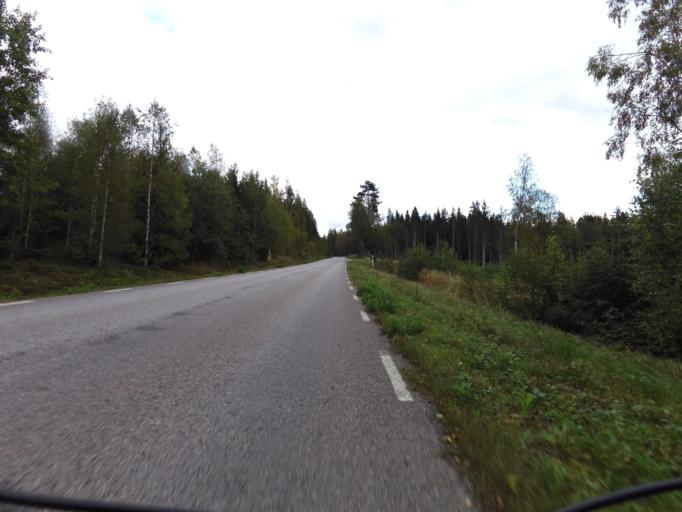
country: SE
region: Gaevleborg
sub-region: Sandvikens Kommun
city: Sandviken
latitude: 60.6507
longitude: 16.8264
